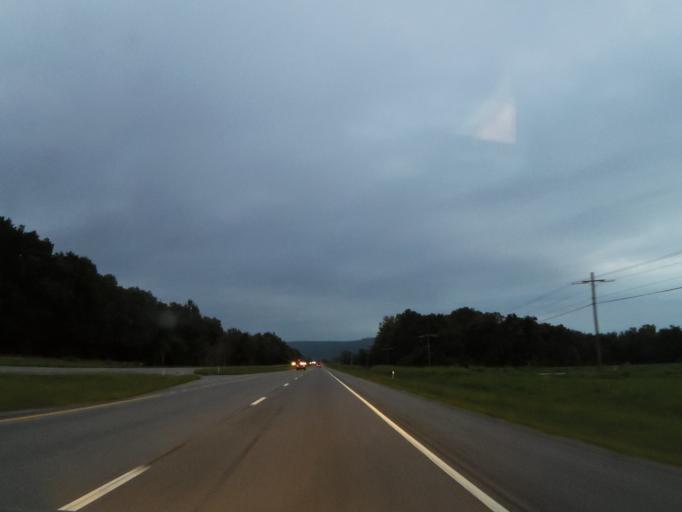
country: US
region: Alabama
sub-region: Madison County
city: Owens Cross Roads
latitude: 34.7220
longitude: -86.4132
